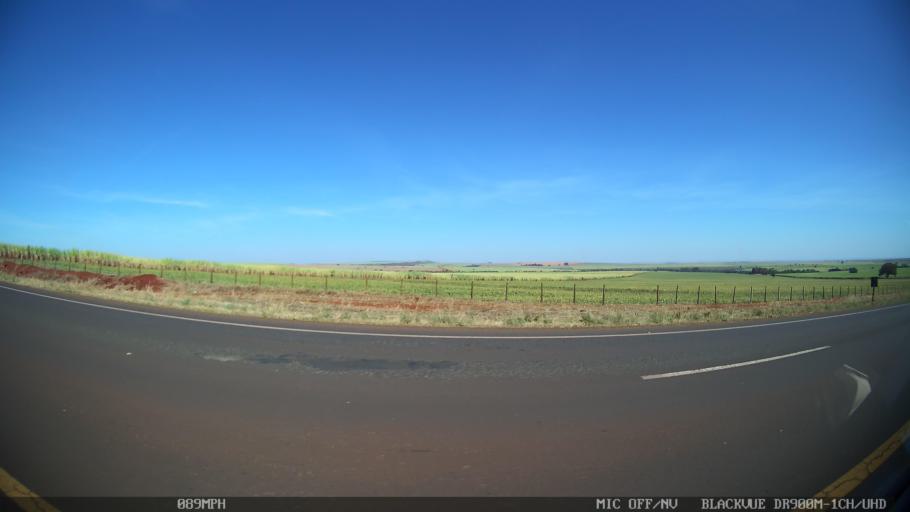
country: BR
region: Sao Paulo
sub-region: Ipua
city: Ipua
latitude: -20.4710
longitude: -48.1095
